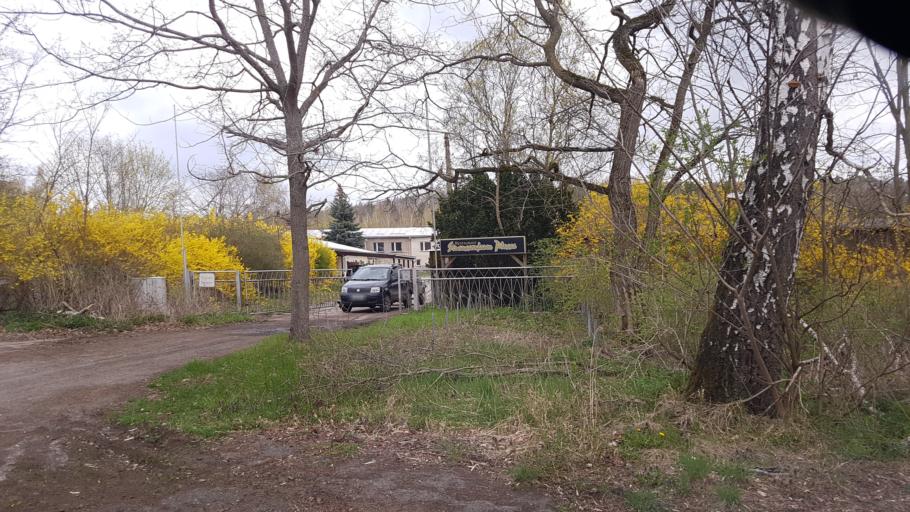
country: DE
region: Brandenburg
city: Plessa
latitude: 51.4741
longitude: 13.6076
